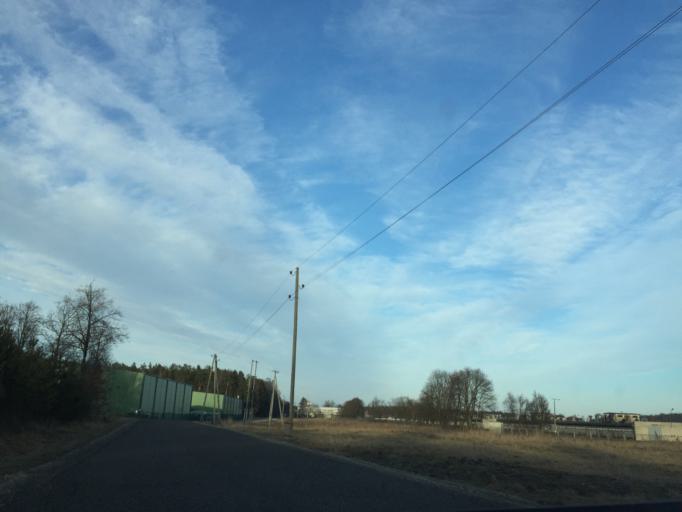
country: LV
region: Kekava
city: Kekava
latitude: 56.8240
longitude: 24.1900
